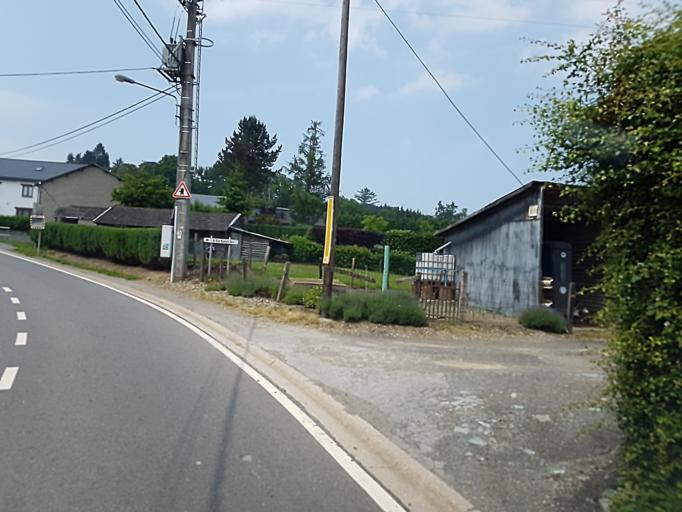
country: BE
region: Wallonia
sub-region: Province de Liege
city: Lierneux
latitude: 50.3226
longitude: 5.7365
